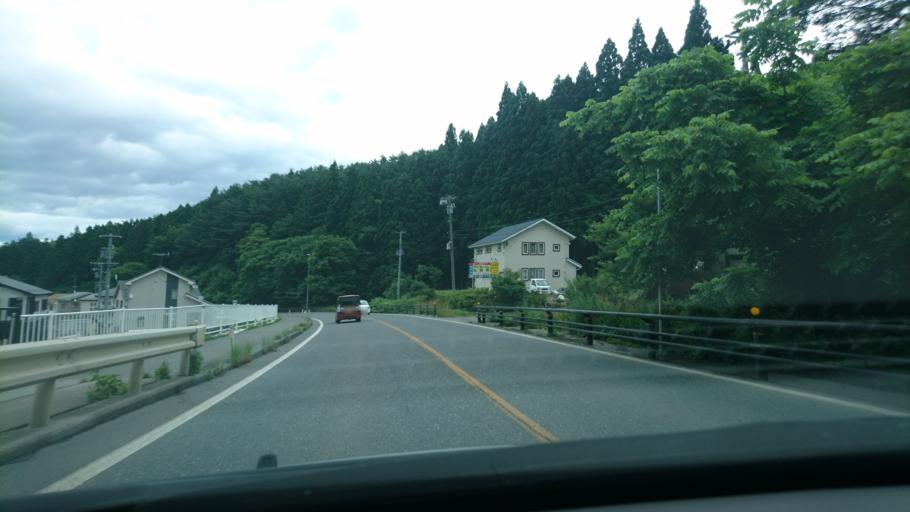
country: JP
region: Iwate
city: Otsuchi
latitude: 39.3662
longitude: 141.9322
